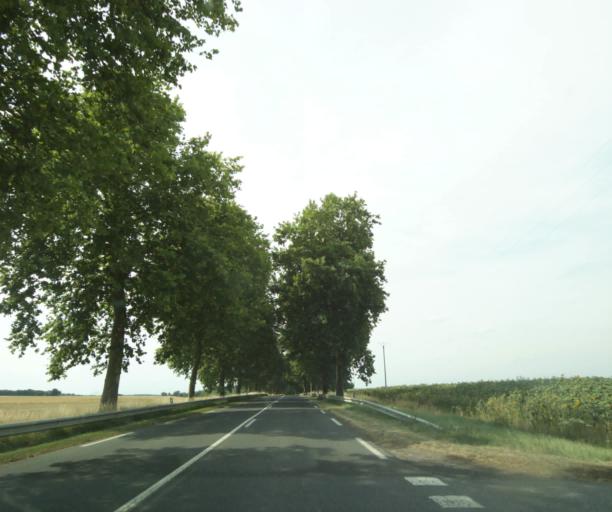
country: FR
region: Centre
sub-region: Departement d'Indre-et-Loire
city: Saint-Paterne-Racan
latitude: 47.6063
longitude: 0.5138
